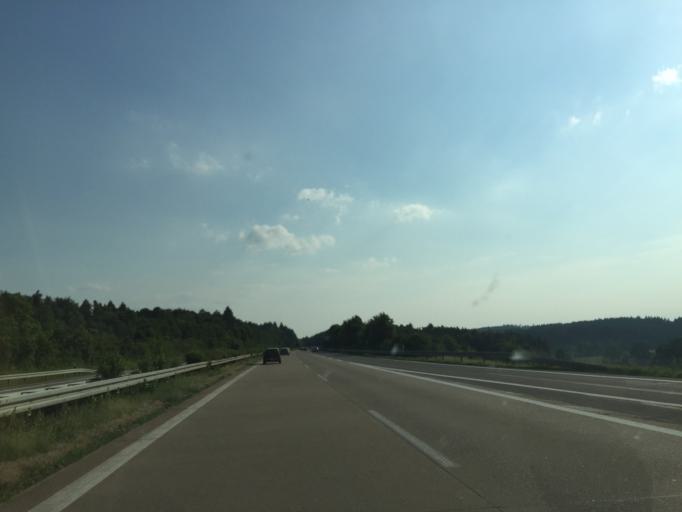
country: DE
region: Baden-Wuerttemberg
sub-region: Karlsruhe Region
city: Rosenberg
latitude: 49.4547
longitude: 9.5315
